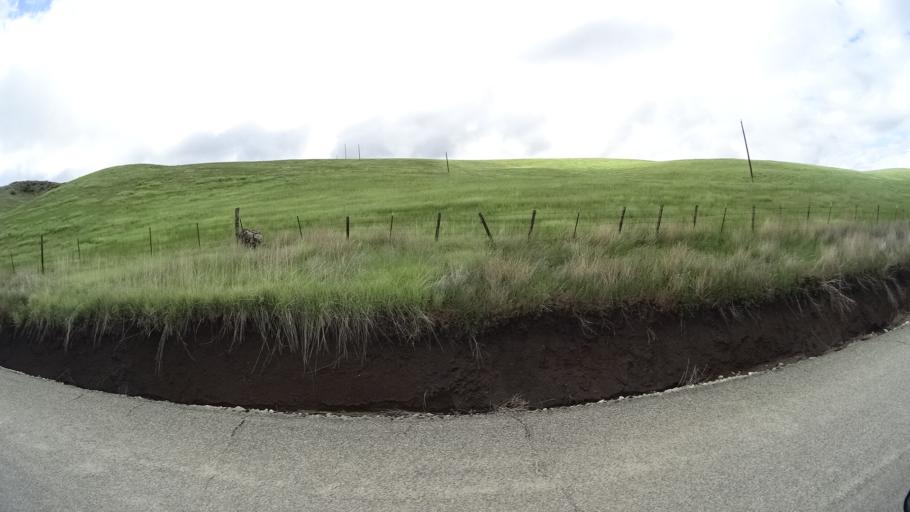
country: US
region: Idaho
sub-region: Ada County
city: Garden City
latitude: 43.7365
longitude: -116.2269
